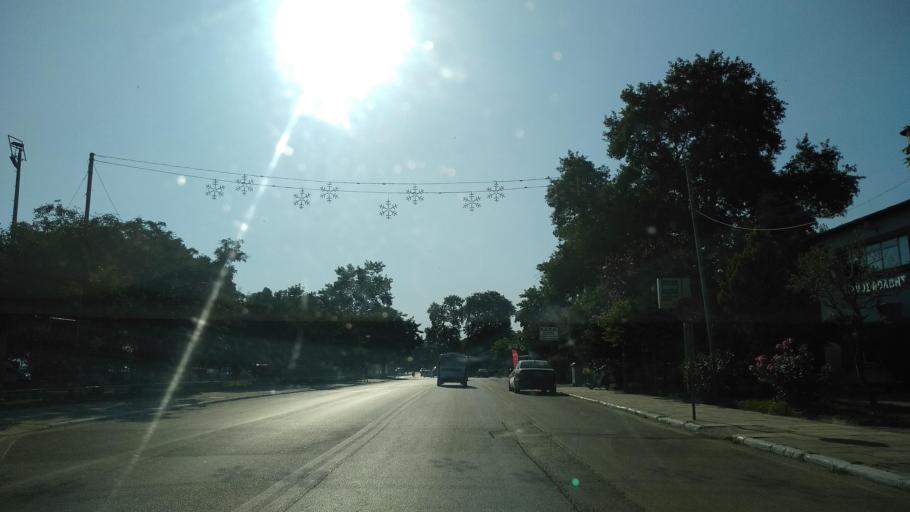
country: GR
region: Central Macedonia
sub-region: Nomos Thessalonikis
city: Stavros
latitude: 40.6652
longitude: 23.6969
